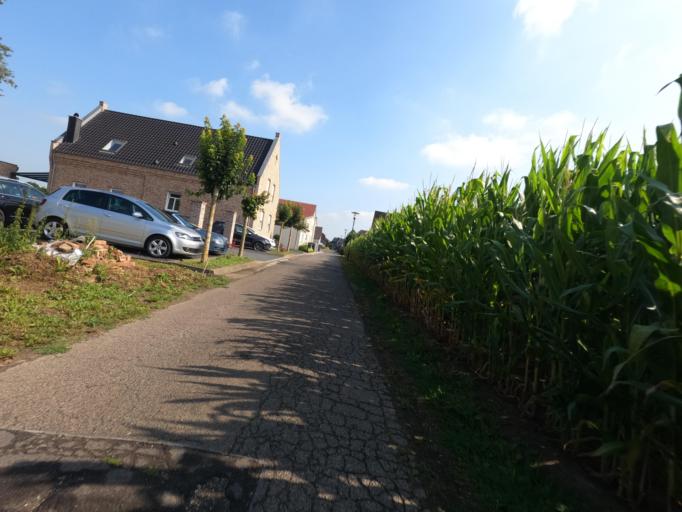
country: DE
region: North Rhine-Westphalia
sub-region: Regierungsbezirk Koln
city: Heinsberg
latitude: 51.0919
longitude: 6.0821
